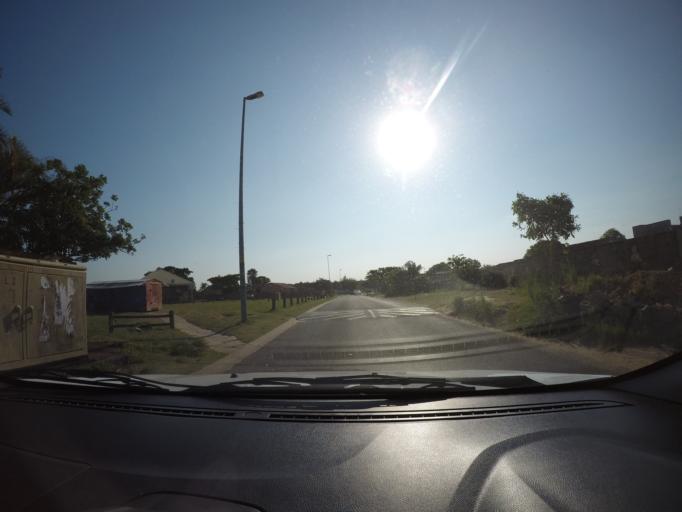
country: ZA
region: KwaZulu-Natal
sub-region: uThungulu District Municipality
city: Richards Bay
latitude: -28.7151
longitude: 32.0362
